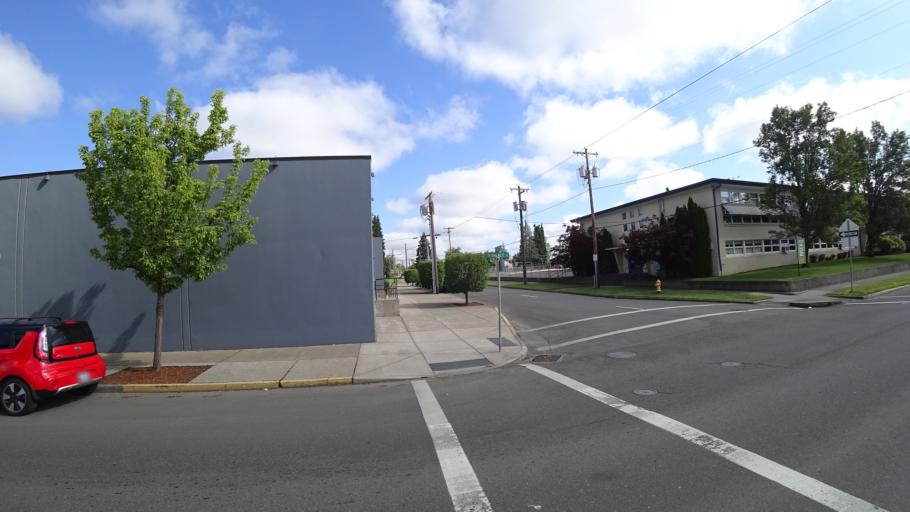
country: US
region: Oregon
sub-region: Washington County
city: Hillsboro
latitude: 45.5175
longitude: -122.9883
